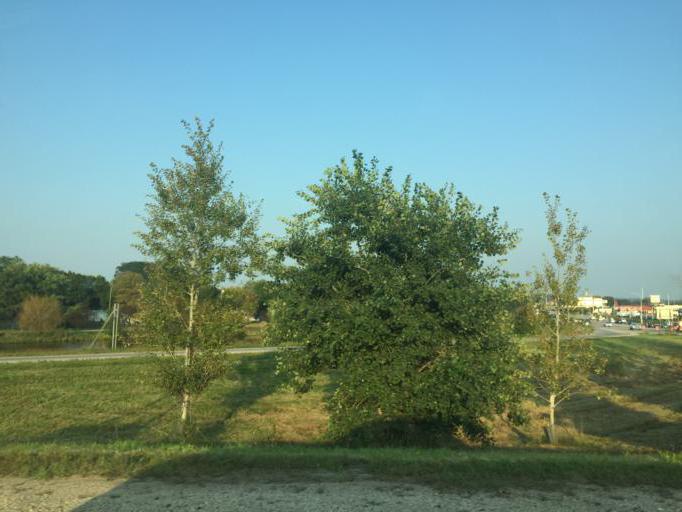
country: US
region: Minnesota
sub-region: Olmsted County
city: Rochester
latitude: 44.0073
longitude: -92.4811
